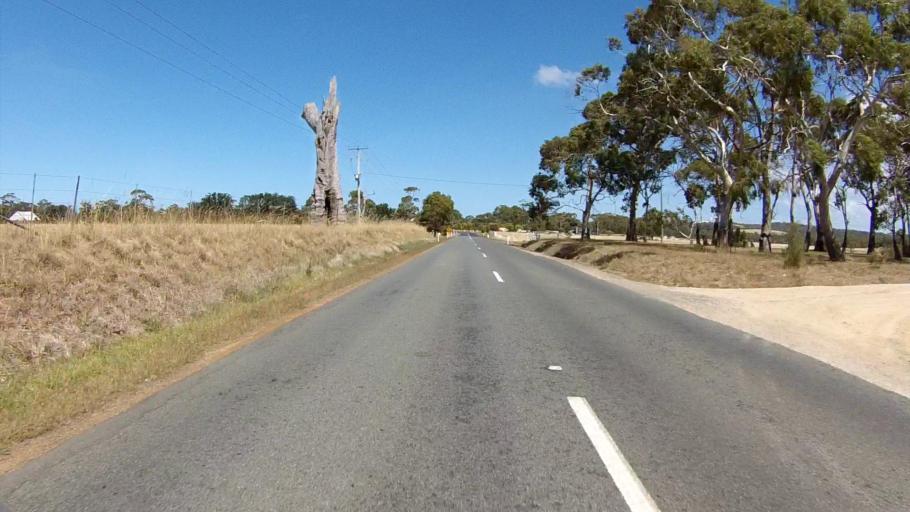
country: AU
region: Tasmania
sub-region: Break O'Day
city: St Helens
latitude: -42.1116
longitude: 148.0560
